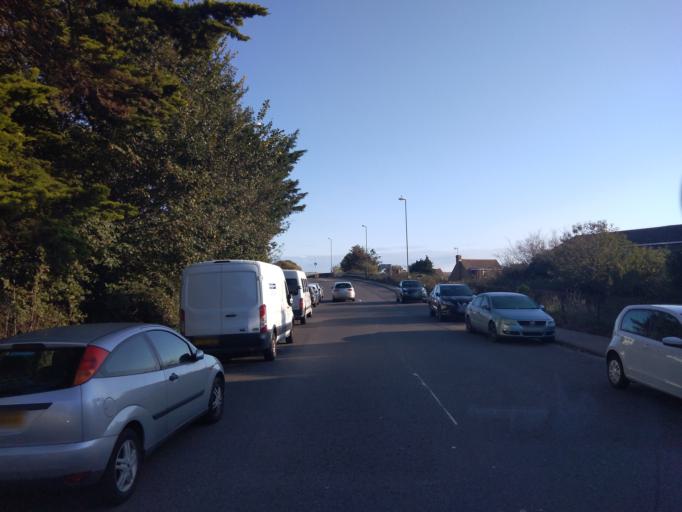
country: GB
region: England
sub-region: West Sussex
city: Lancing
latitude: 50.8262
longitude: -0.3218
